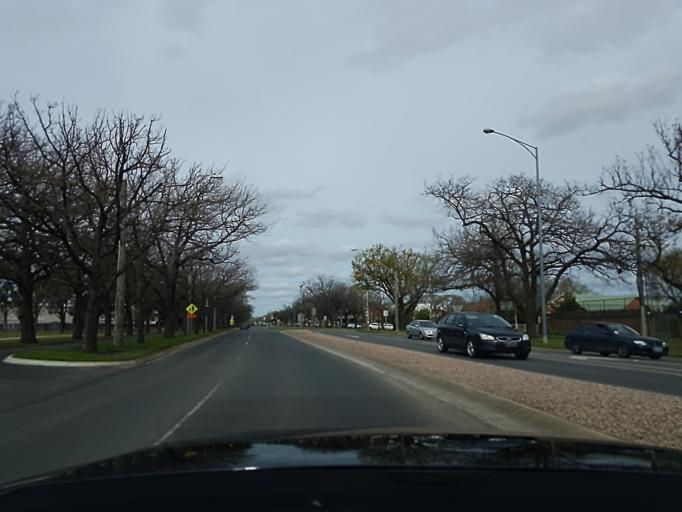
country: AU
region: Victoria
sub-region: Ballarat North
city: Newington
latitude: -37.5536
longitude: 143.8142
